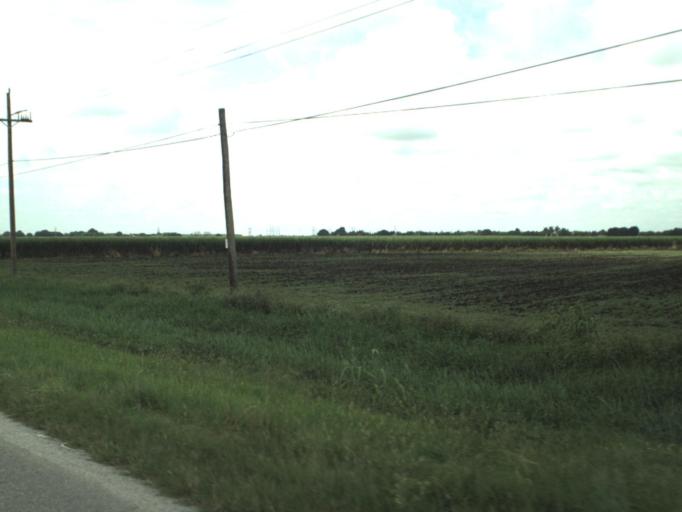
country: US
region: Florida
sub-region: Palm Beach County
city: Belle Glade
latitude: 26.7145
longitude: -80.6841
